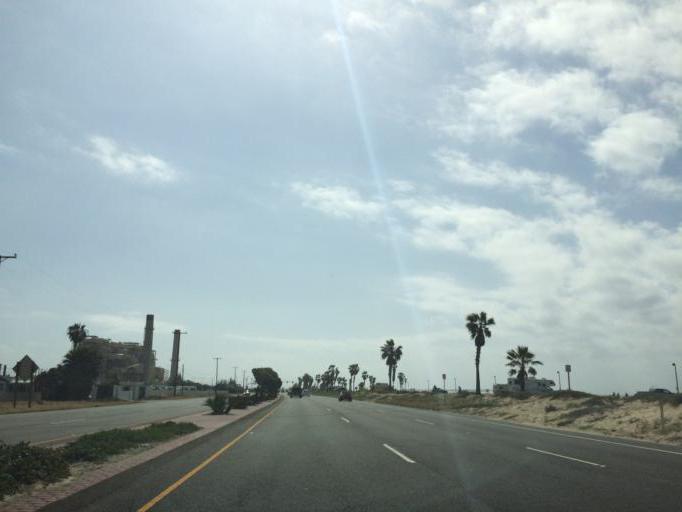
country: US
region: California
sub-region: Orange County
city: Huntington Beach
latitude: 33.6463
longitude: -117.9848
